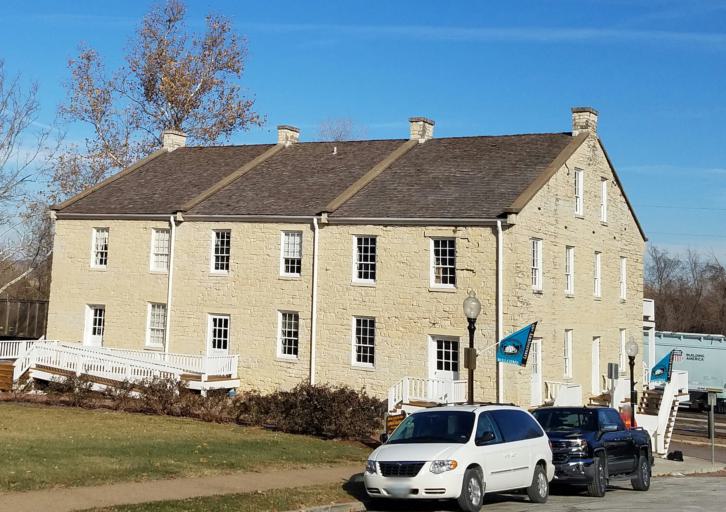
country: US
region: Missouri
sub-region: Cole County
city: Jefferson City
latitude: 38.5785
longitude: -92.1721
